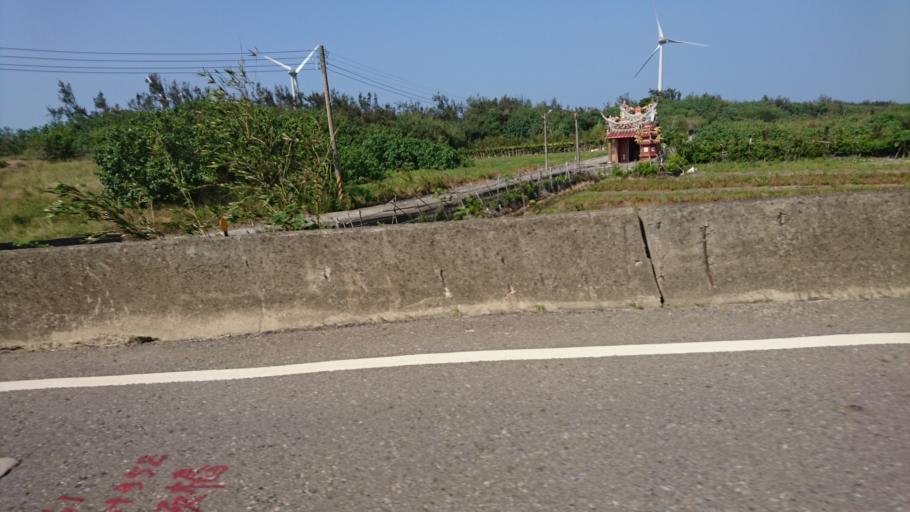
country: TW
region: Taiwan
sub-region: Miaoli
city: Miaoli
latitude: 24.6635
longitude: 120.8213
